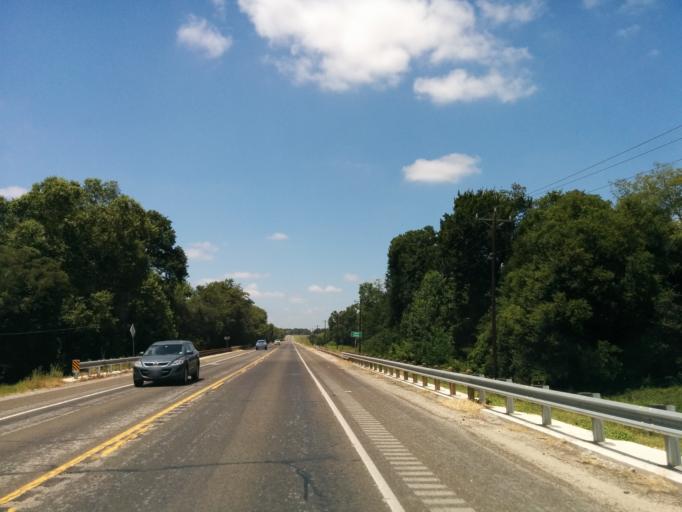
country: US
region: Texas
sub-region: Madison County
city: Madisonville
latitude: 30.9375
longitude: -95.9347
